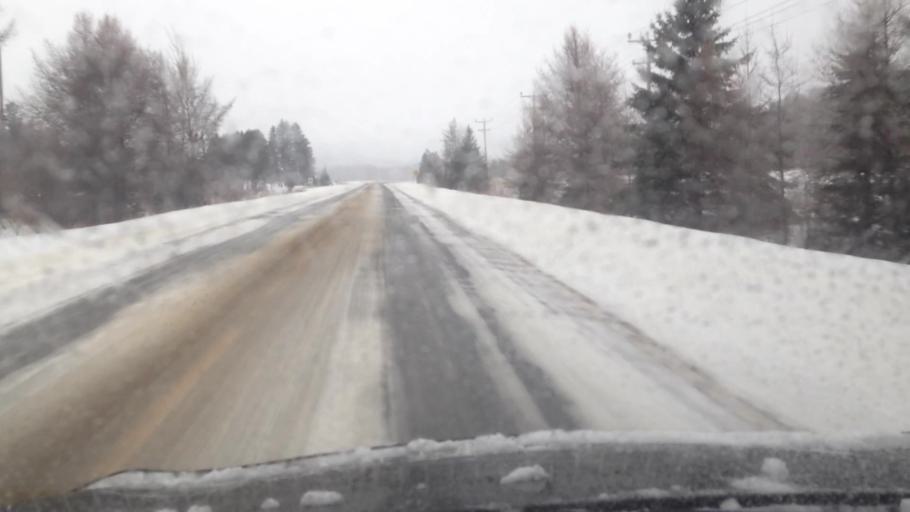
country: CA
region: Quebec
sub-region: Laurentides
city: Mont-Tremblant
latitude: 46.0566
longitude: -74.6183
